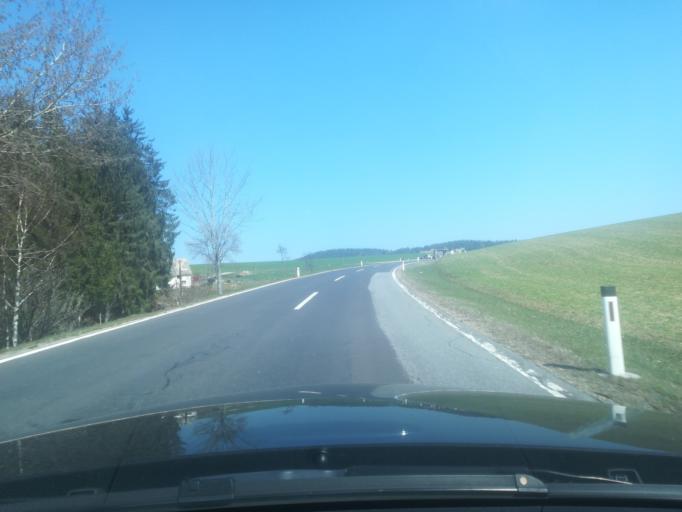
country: AT
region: Upper Austria
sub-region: Politischer Bezirk Perg
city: Bad Kreuzen
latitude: 48.4122
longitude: 14.7283
